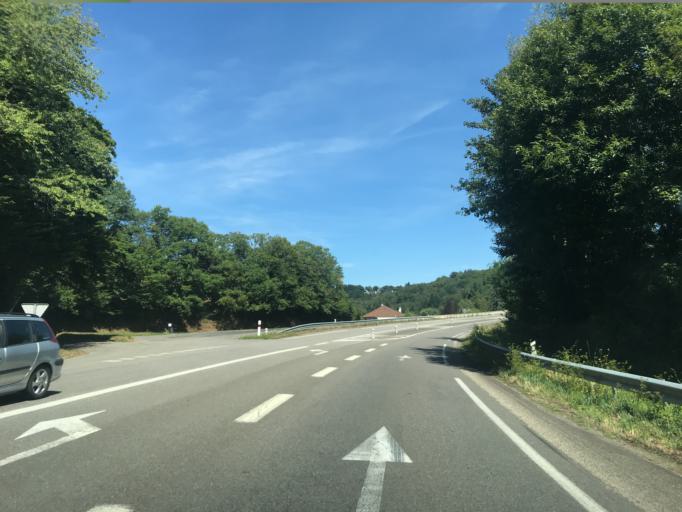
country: FR
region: Limousin
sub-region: Departement de la Correze
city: Naves
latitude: 45.2943
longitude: 1.8078
